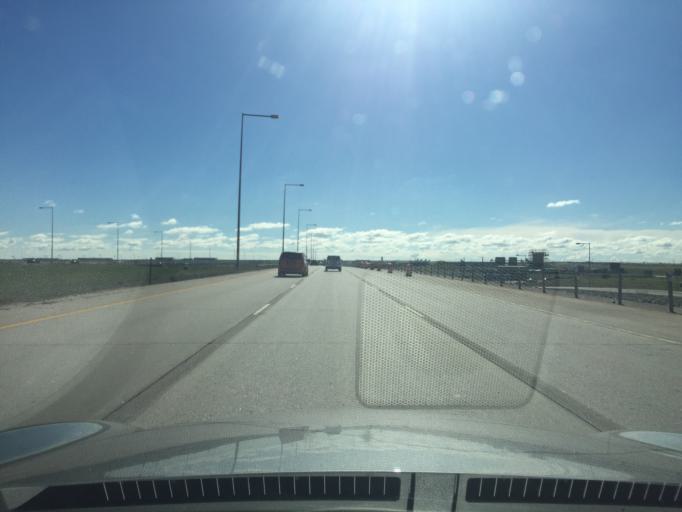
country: US
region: Colorado
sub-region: Adams County
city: Aurora
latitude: 39.8335
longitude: -104.6958
